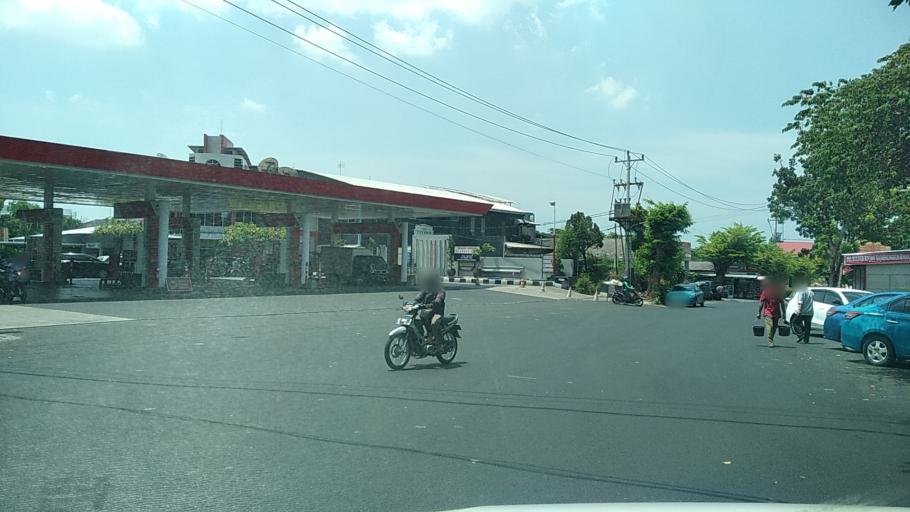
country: ID
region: Central Java
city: Semarang
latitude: -7.0046
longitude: 110.4097
